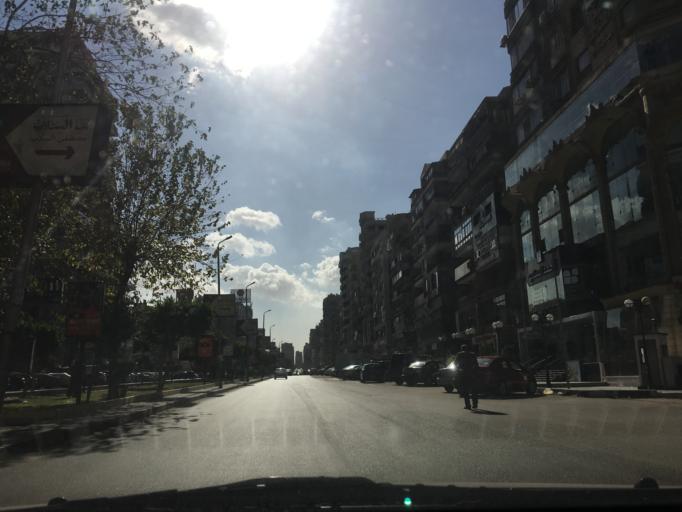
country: EG
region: Muhafazat al Qahirah
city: Cairo
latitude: 30.0582
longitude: 31.3456
